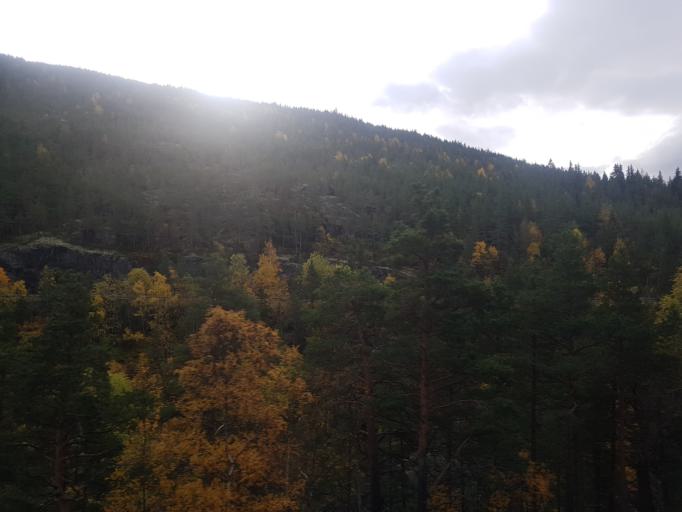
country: NO
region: Oppland
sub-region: Sel
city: Otta
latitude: 61.8782
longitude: 9.4079
